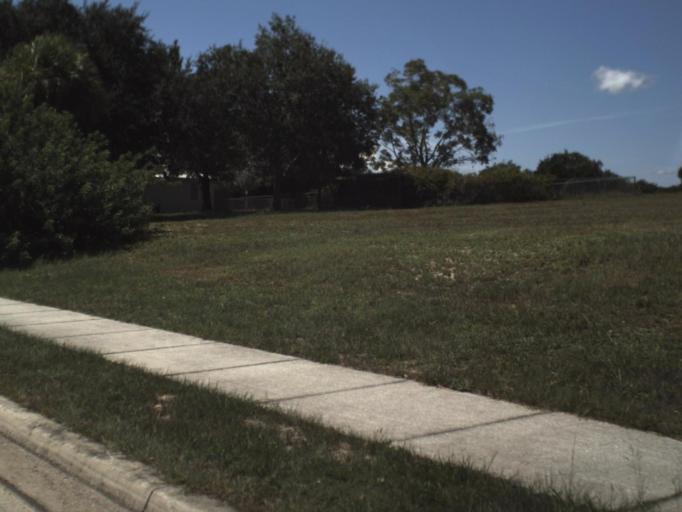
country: US
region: Florida
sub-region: Polk County
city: Frostproof
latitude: 27.7543
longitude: -81.5306
